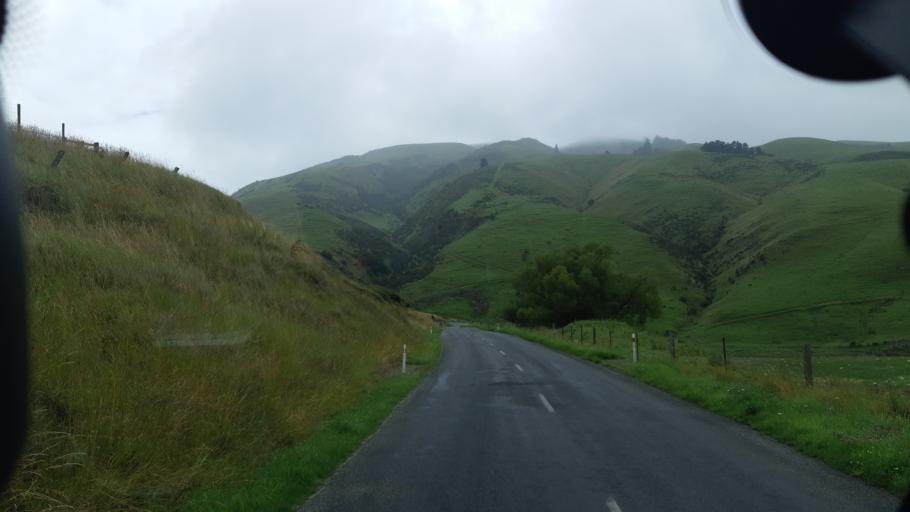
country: NZ
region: Canterbury
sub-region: Timaru District
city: Pleasant Point
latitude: -44.4007
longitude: 171.0082
